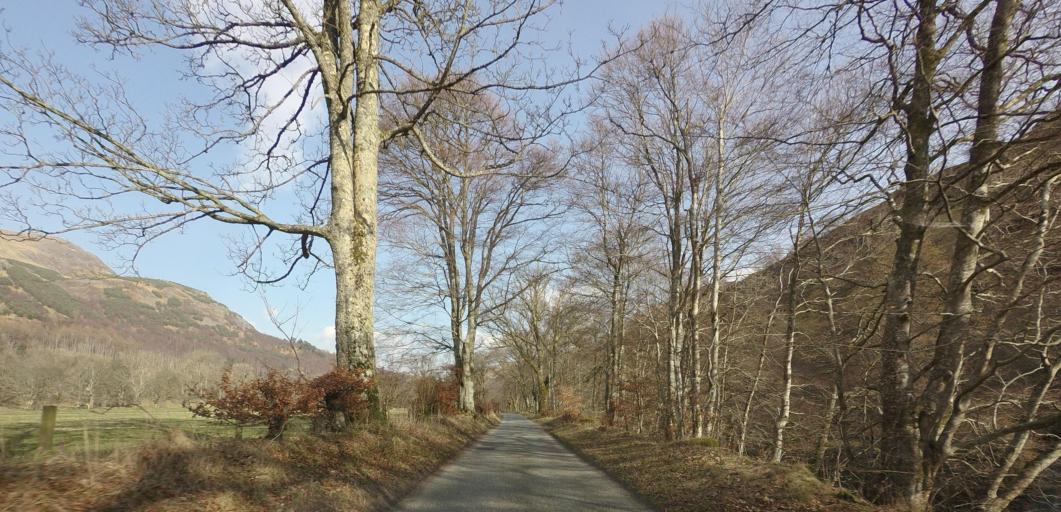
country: GB
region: Scotland
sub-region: Perth and Kinross
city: Comrie
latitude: 56.5989
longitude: -4.1304
